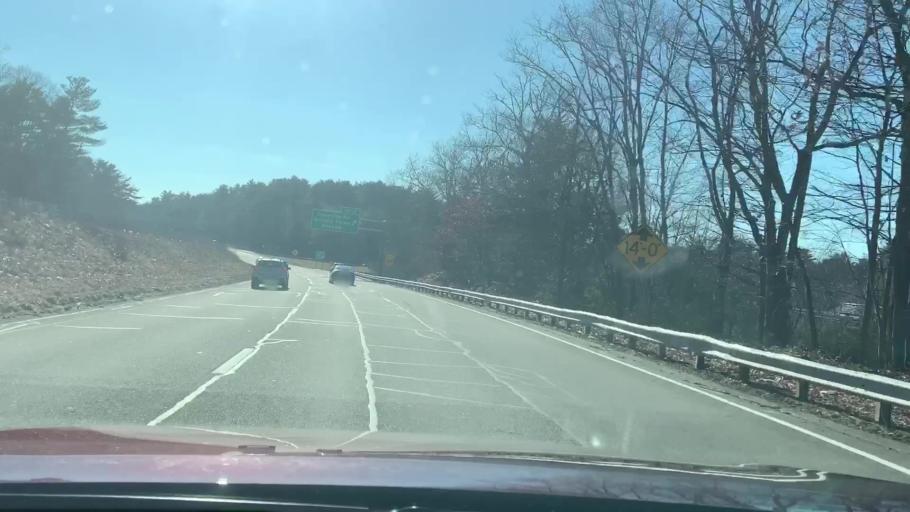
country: US
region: Massachusetts
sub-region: Essex County
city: Beverly Cove
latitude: 42.5868
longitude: -70.8184
